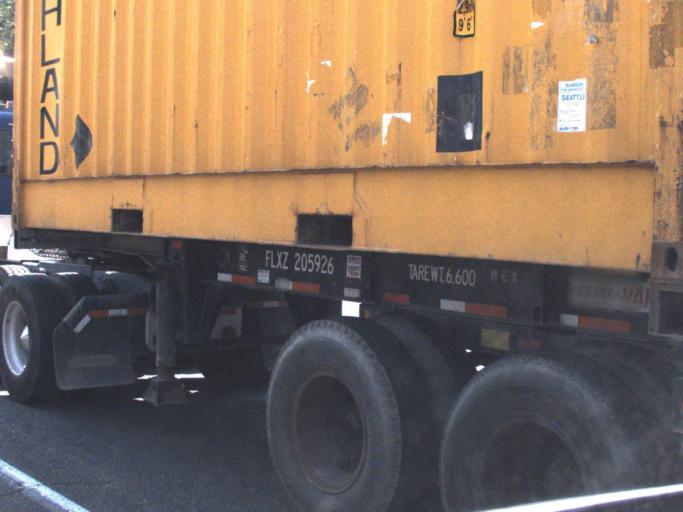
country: US
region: Washington
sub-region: King County
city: White Center
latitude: 47.5355
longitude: -122.3332
